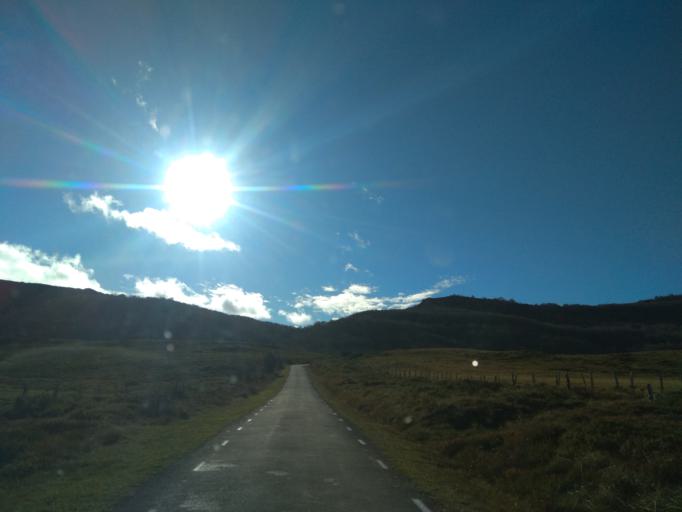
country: ES
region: Cantabria
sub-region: Provincia de Cantabria
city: San Martin de Elines
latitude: 42.9453
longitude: -3.8228
